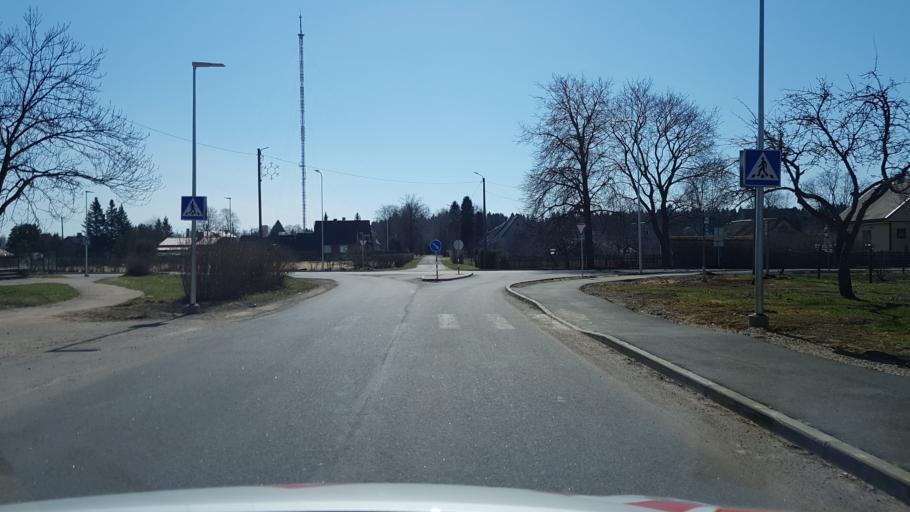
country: EE
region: Ida-Virumaa
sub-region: Kohtla-Nomme vald
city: Kohtla-Nomme
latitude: 59.3544
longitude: 27.1917
